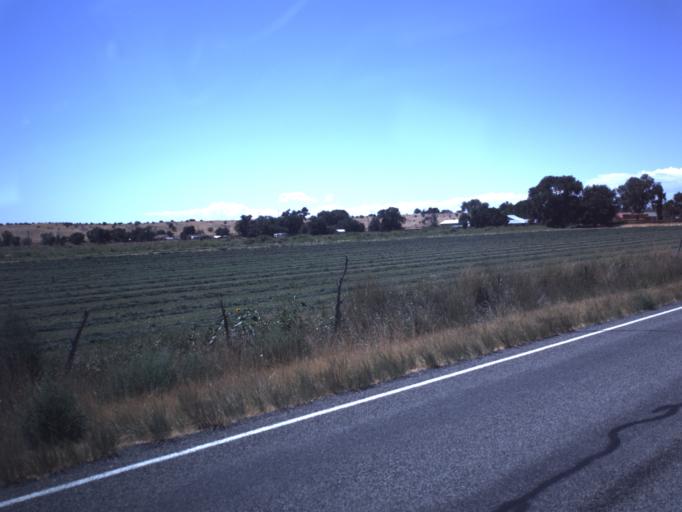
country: US
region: Utah
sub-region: Millard County
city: Delta
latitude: 39.5366
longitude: -112.2689
